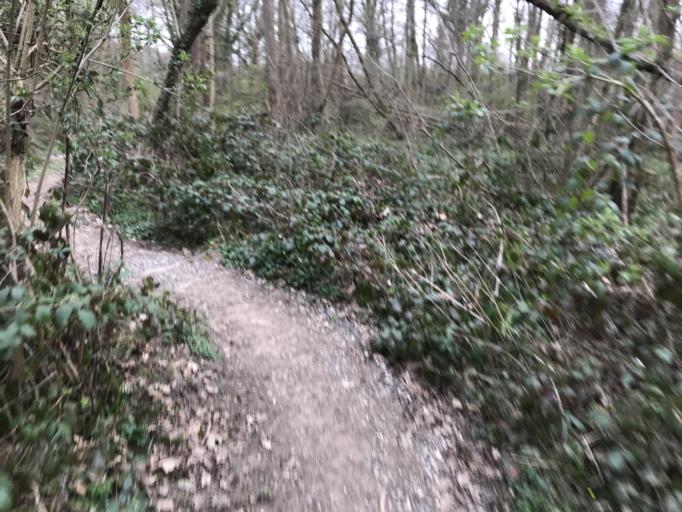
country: FR
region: Ile-de-France
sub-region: Departement de l'Essonne
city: Limours
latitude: 48.6513
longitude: 2.0476
